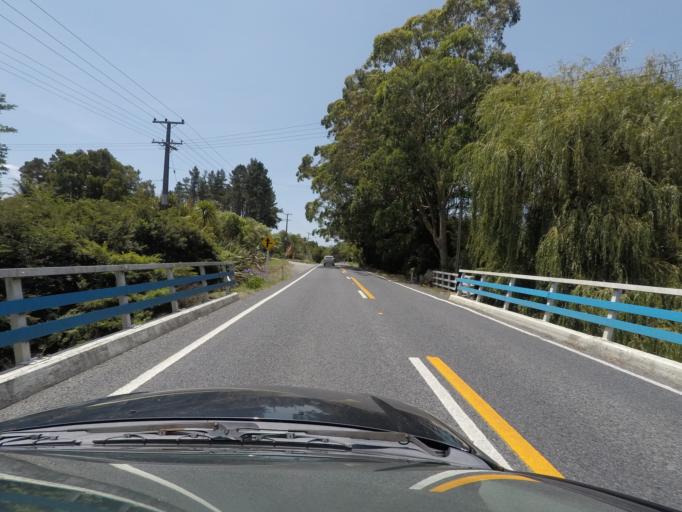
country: NZ
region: Auckland
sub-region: Auckland
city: Warkworth
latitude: -36.3711
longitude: 174.7047
